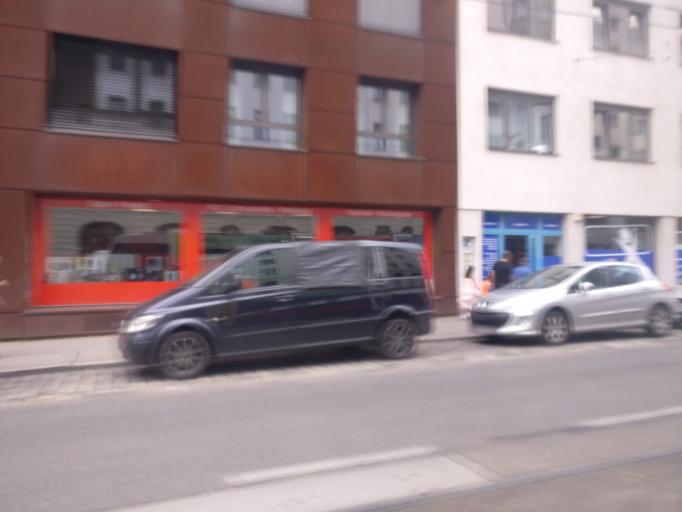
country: AT
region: Vienna
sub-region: Wien Stadt
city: Vienna
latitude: 48.2342
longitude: 16.3702
